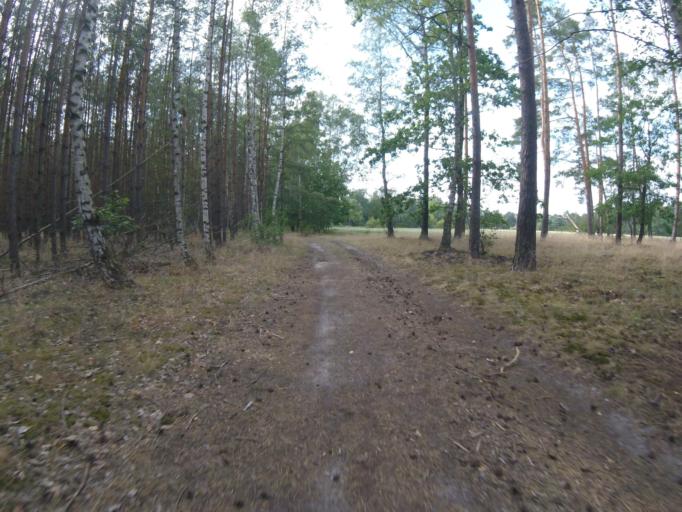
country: DE
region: Brandenburg
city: Wildau
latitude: 52.3095
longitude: 13.7207
